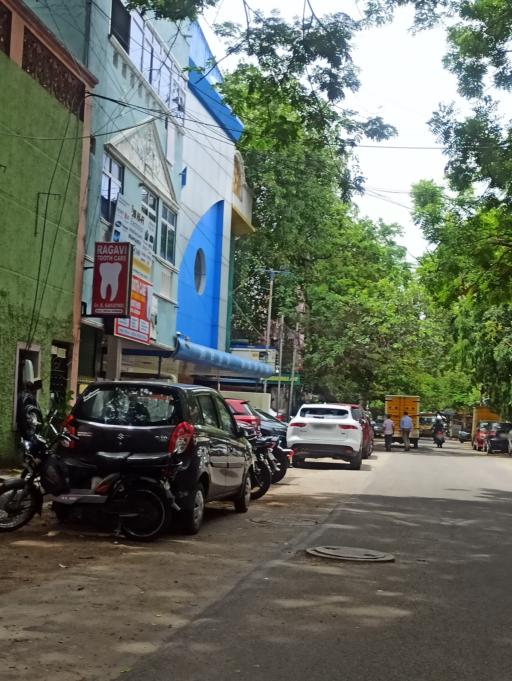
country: IN
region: Tamil Nadu
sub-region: Chennai
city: Chetput
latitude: 13.0541
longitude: 80.2222
